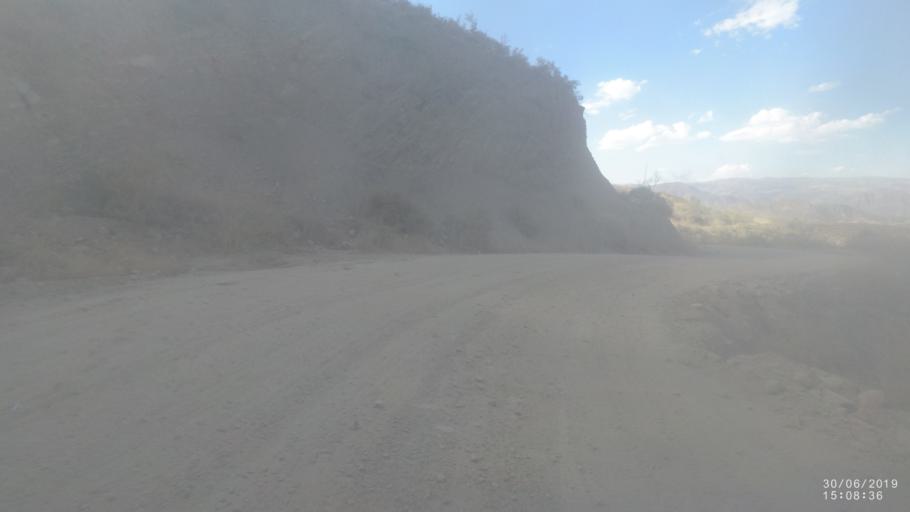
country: BO
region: Cochabamba
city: Irpa Irpa
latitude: -17.7315
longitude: -66.3014
